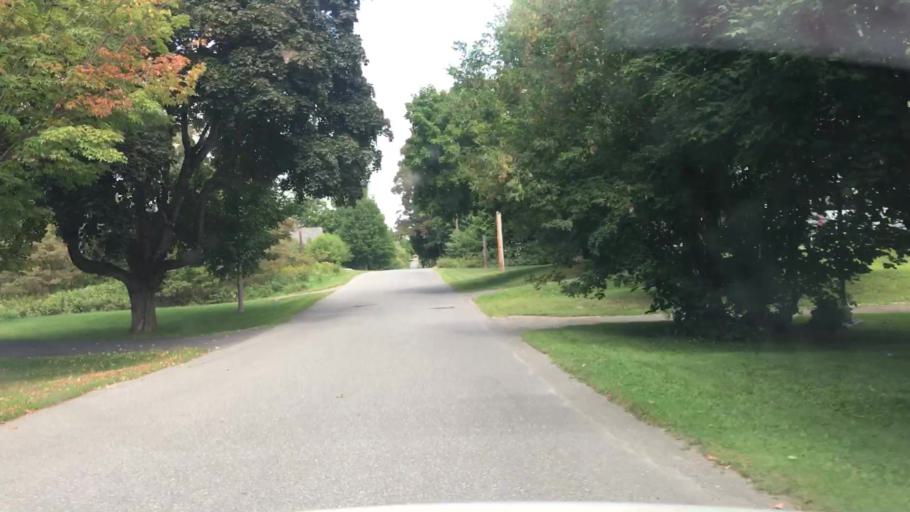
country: US
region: Maine
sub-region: Piscataquis County
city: Dover-Foxcroft
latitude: 45.1859
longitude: -69.2217
